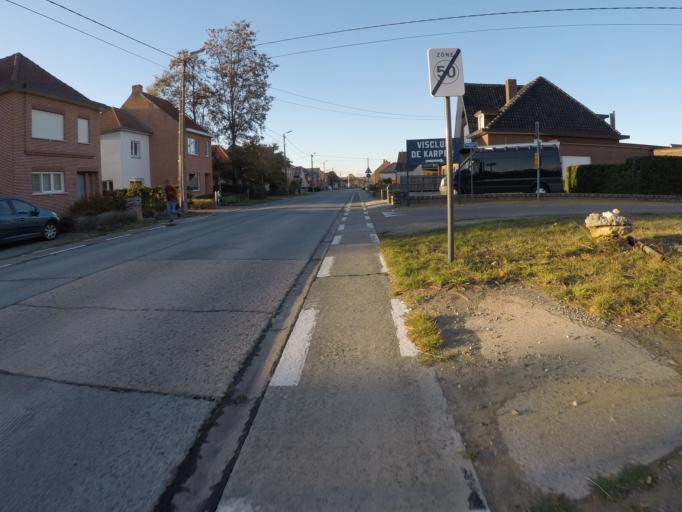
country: BE
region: Flanders
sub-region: Provincie Vlaams-Brabant
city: Begijnendijk
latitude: 51.0251
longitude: 4.7998
